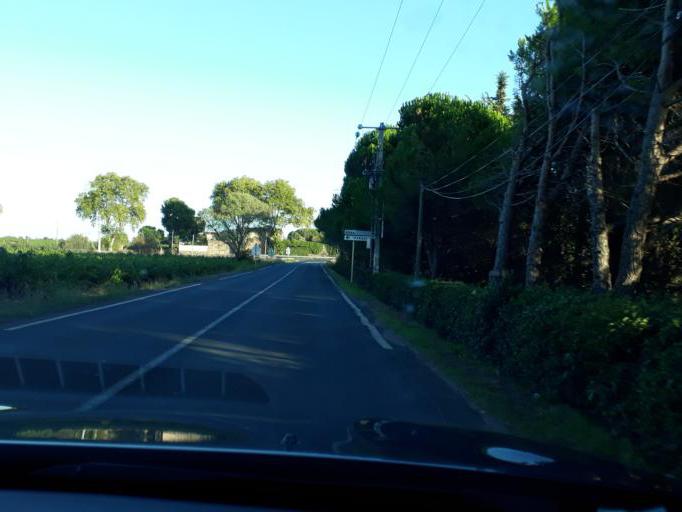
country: FR
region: Languedoc-Roussillon
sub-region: Departement de l'Herault
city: Agde
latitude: 43.3303
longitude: 3.4829
